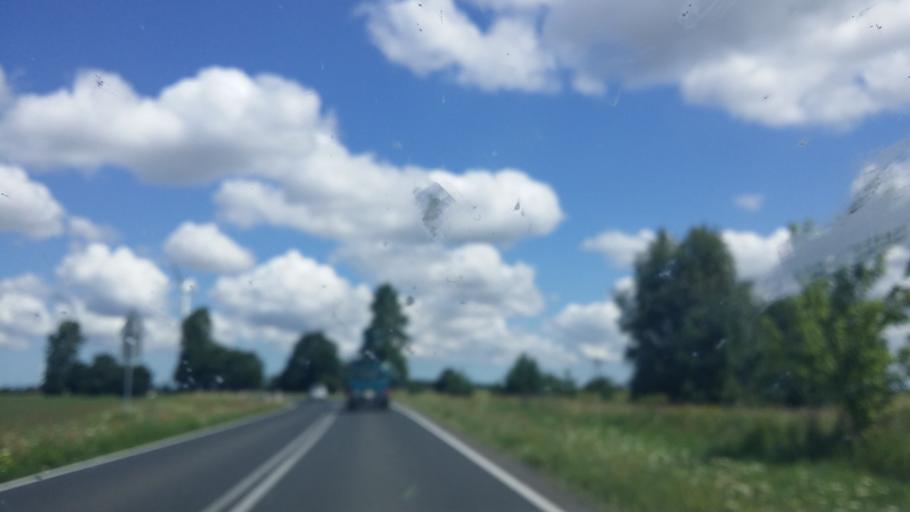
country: PL
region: West Pomeranian Voivodeship
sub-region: Powiat kolobrzeski
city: Goscino
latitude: 53.9764
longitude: 15.6732
